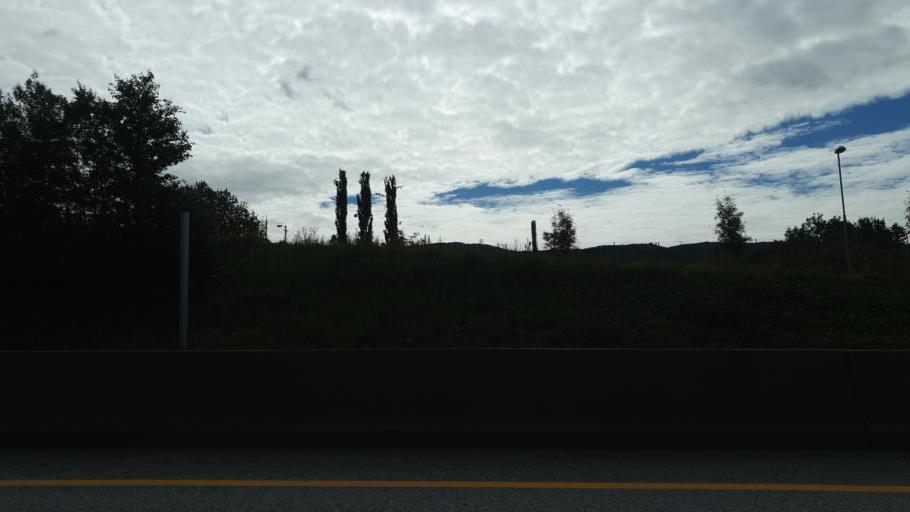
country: NO
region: Sor-Trondelag
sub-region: Melhus
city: Melhus
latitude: 63.2968
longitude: 10.2822
